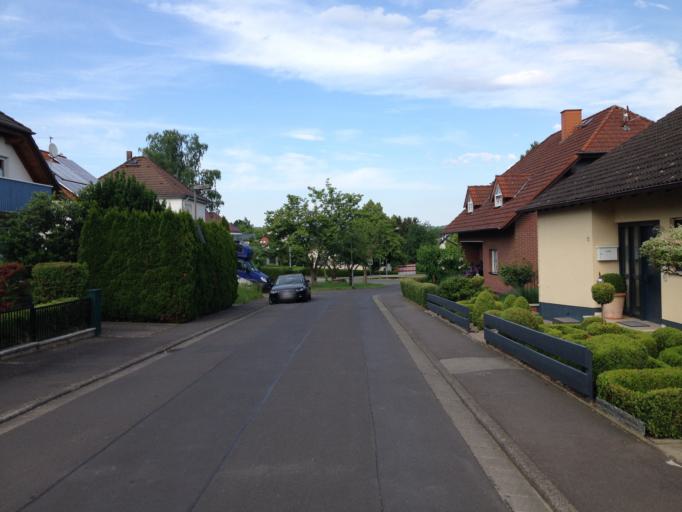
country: DE
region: Hesse
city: Staufenberg
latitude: 50.6600
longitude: 8.7301
